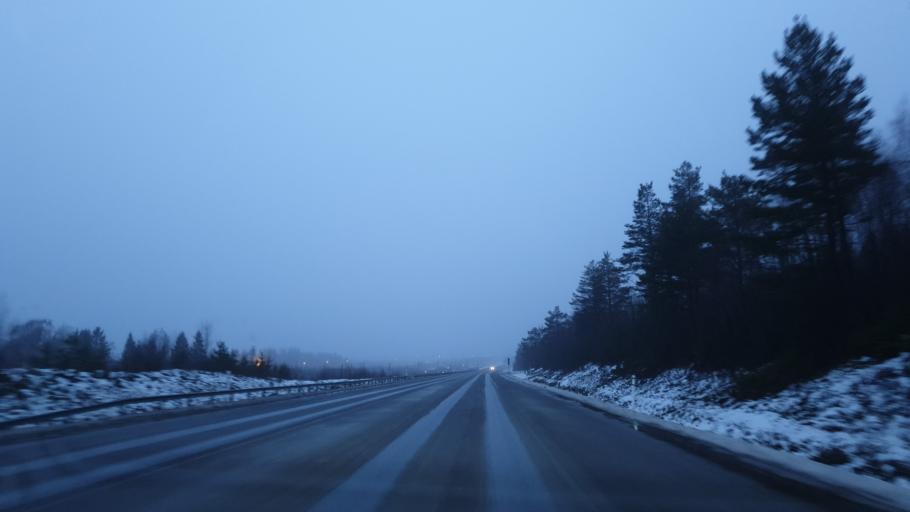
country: SE
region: Vaesterbotten
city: Obbola
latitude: 63.7784
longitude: 20.3256
